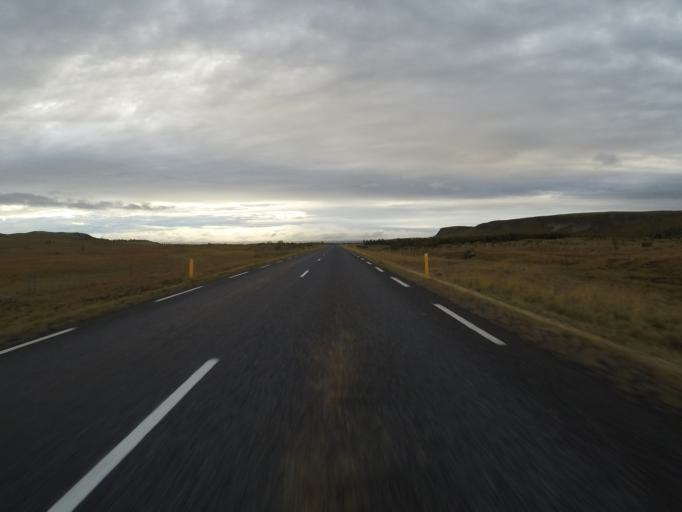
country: IS
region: South
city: Vestmannaeyjar
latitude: 64.0421
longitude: -20.1932
